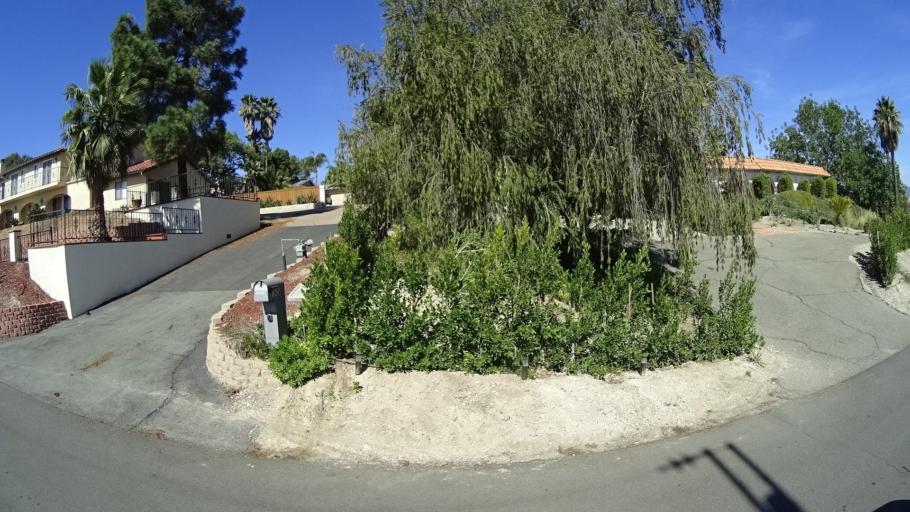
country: US
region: California
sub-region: San Diego County
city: Casa de Oro-Mount Helix
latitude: 32.7472
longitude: -116.9675
